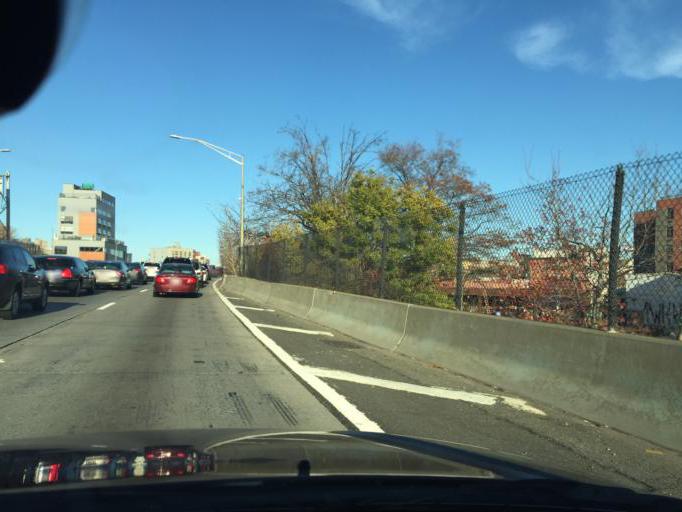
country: US
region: New York
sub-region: Queens County
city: Long Island City
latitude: 40.7131
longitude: -73.9539
